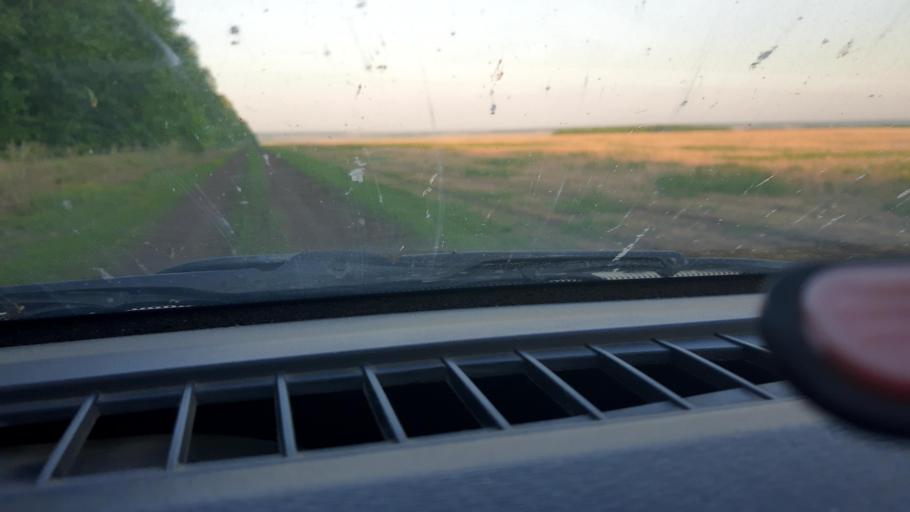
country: RU
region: Bashkortostan
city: Asanovo
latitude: 54.8710
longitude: 55.5307
